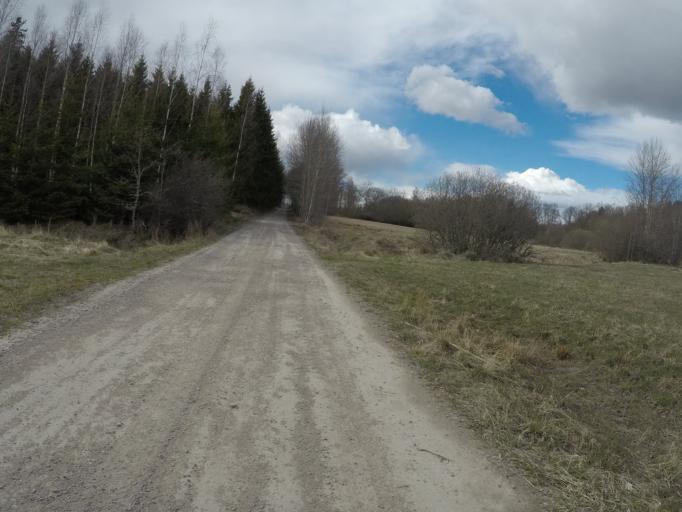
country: SE
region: Soedermanland
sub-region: Eskilstuna Kommun
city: Kvicksund
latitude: 59.4723
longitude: 16.3026
